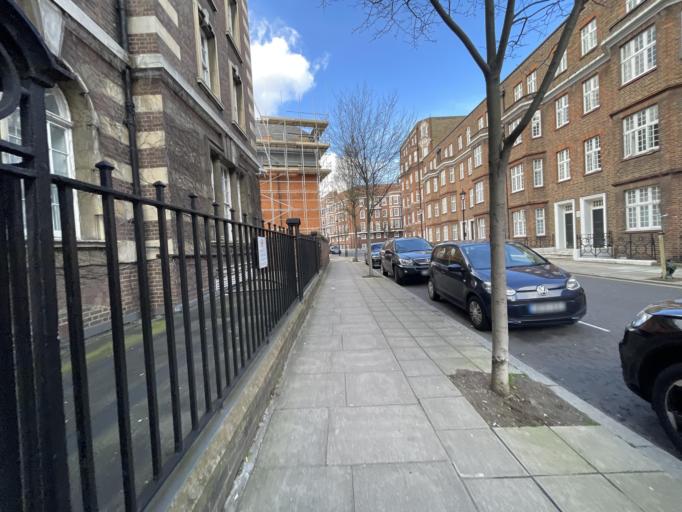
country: GB
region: England
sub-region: Greater London
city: Bayswater
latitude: 51.5172
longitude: -0.1629
